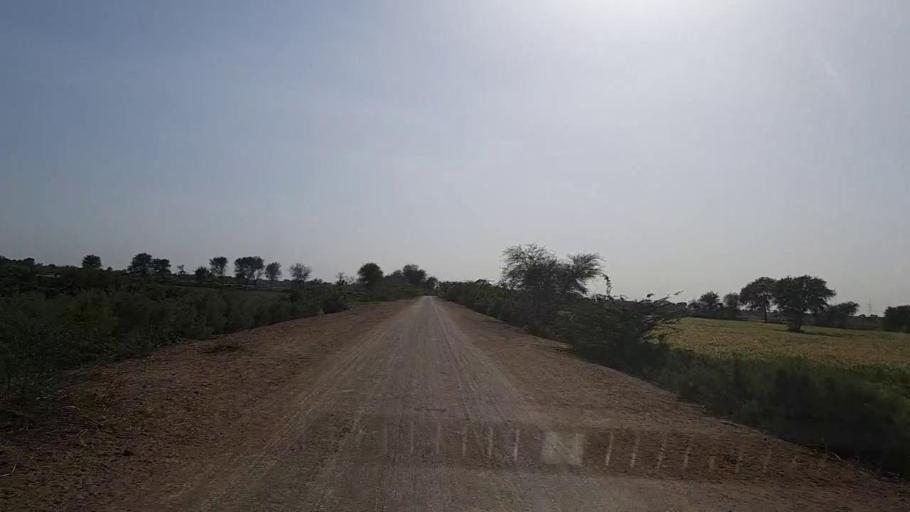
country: PK
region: Sindh
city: Kotri
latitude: 25.1579
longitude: 68.2933
